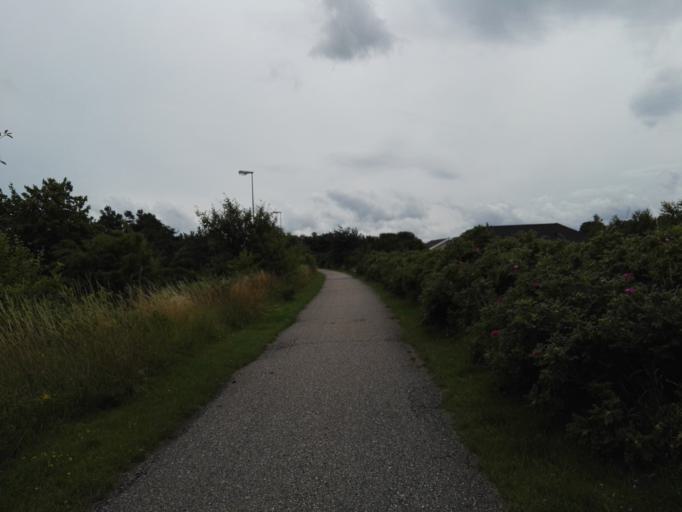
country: DK
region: Capital Region
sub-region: Egedal Kommune
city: Olstykke
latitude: 55.7763
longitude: 12.1615
